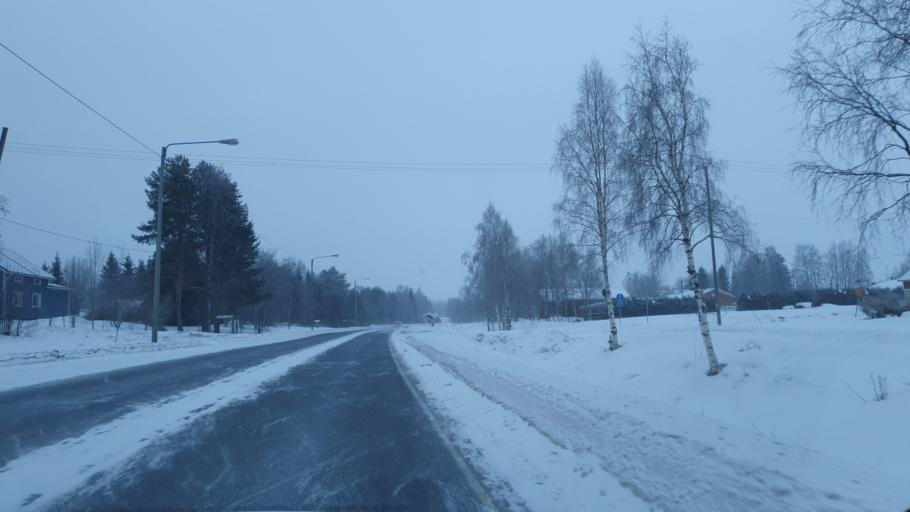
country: FI
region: Lapland
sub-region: Kemi-Tornio
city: Tornio
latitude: 65.9098
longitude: 24.1415
